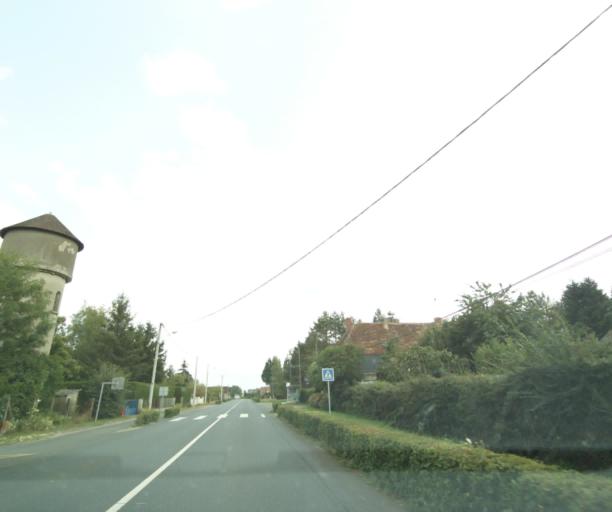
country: FR
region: Centre
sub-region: Departement de l'Indre
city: Buzancais
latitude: 46.8834
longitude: 1.4460
